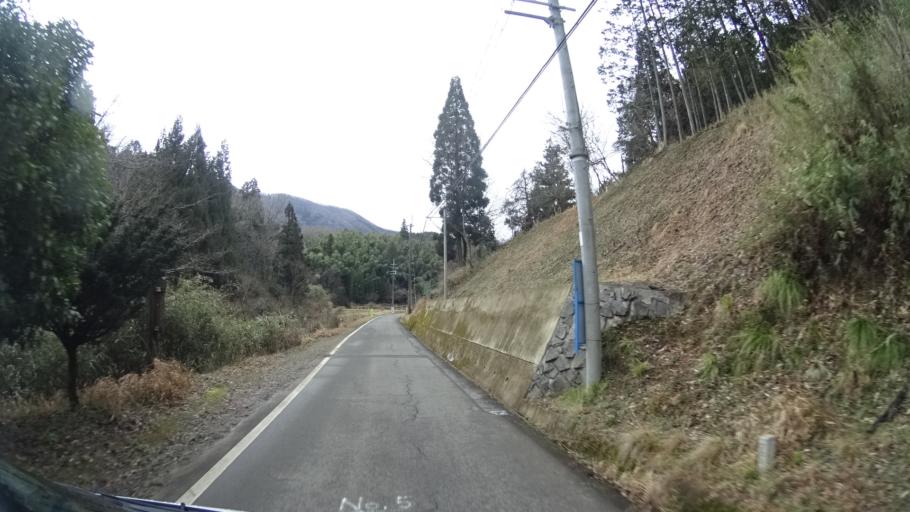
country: JP
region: Kyoto
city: Maizuru
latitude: 35.3781
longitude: 135.3517
